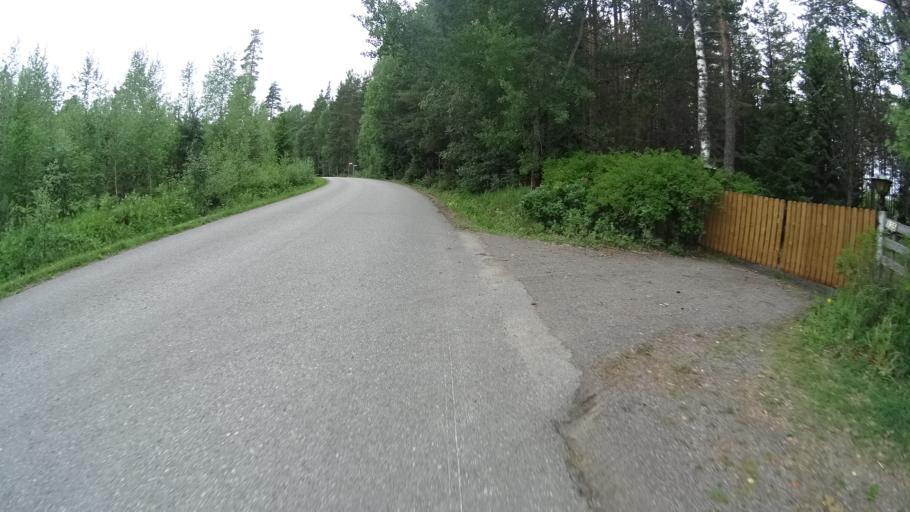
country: FI
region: Uusimaa
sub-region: Helsinki
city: Karkkila
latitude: 60.5959
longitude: 24.1208
